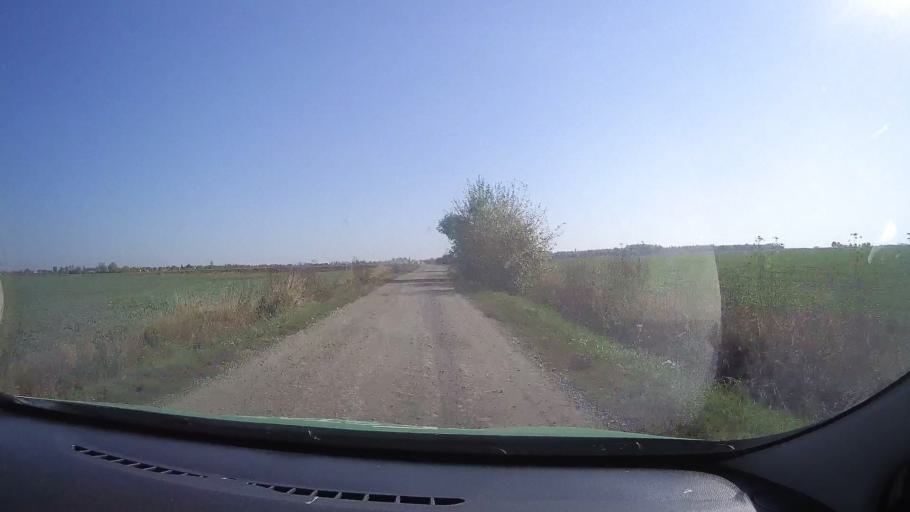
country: RO
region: Satu Mare
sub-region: Comuna Berveni
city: Berveni
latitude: 47.7351
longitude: 22.4529
